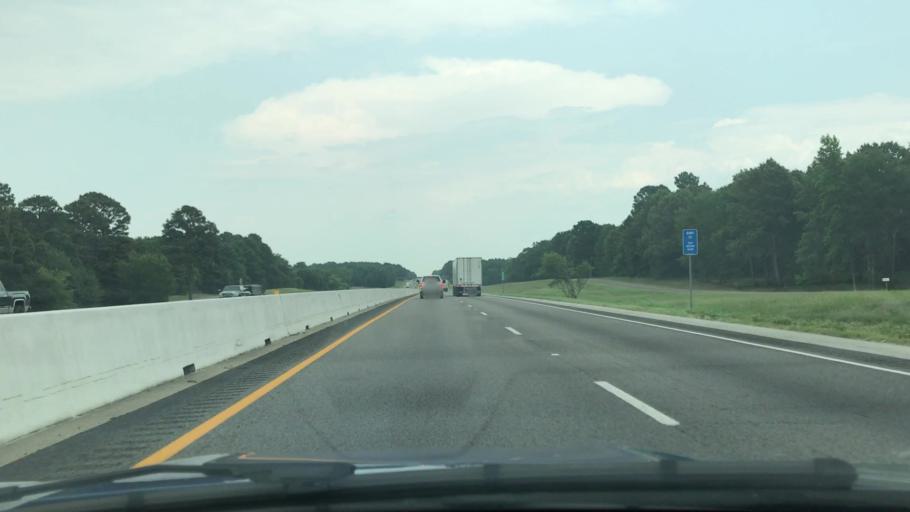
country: US
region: Texas
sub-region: Gregg County
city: Liberty City
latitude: 32.4374
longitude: -95.0212
